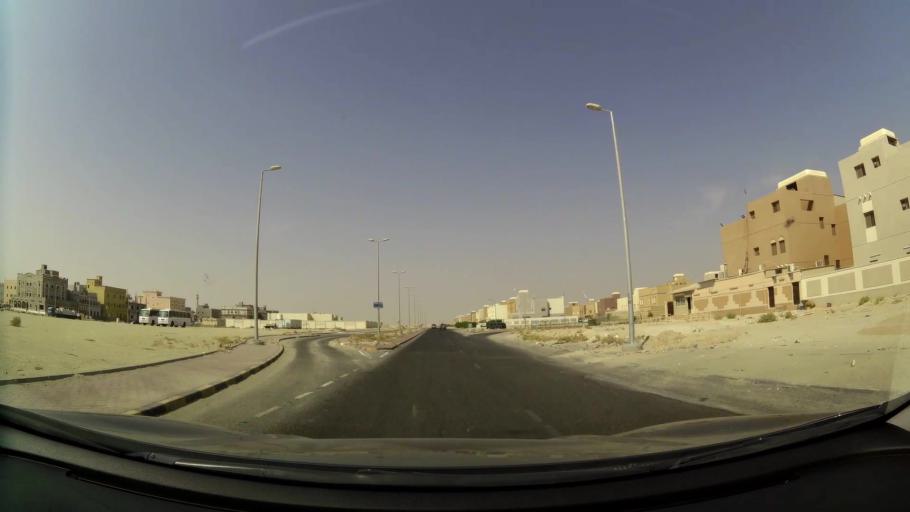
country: KW
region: Al Ahmadi
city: Al Wafrah
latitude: 28.8010
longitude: 48.0526
